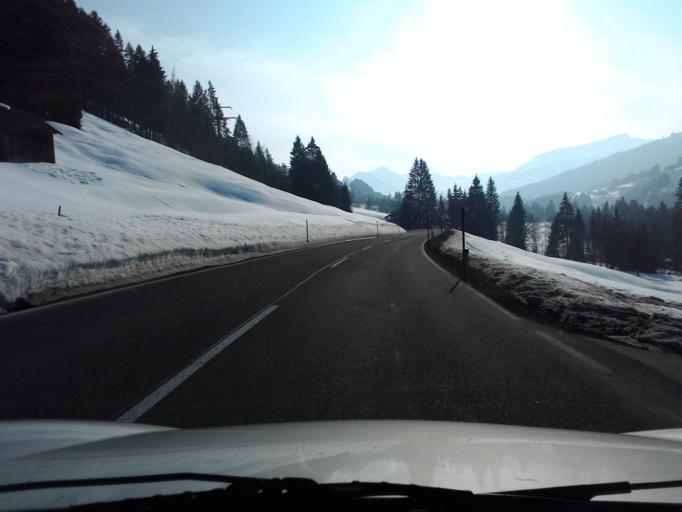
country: DE
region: Bavaria
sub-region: Swabia
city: Oberstdorf
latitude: 47.3824
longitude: 10.2232
